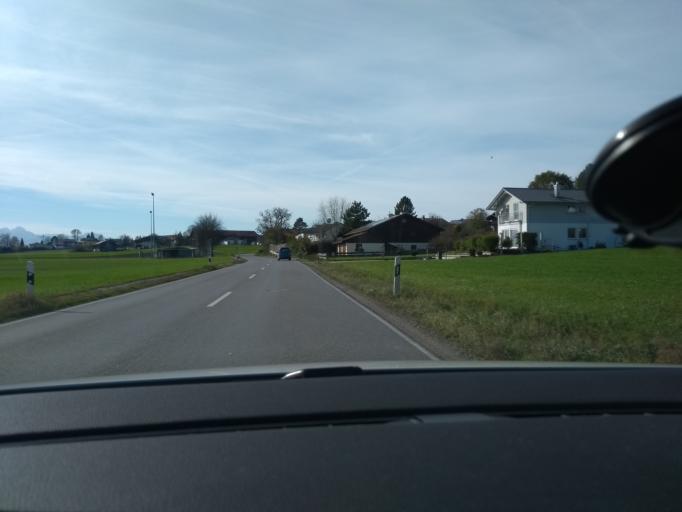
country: DE
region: Bavaria
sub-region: Upper Bavaria
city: Prutting
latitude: 47.8915
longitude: 12.1979
